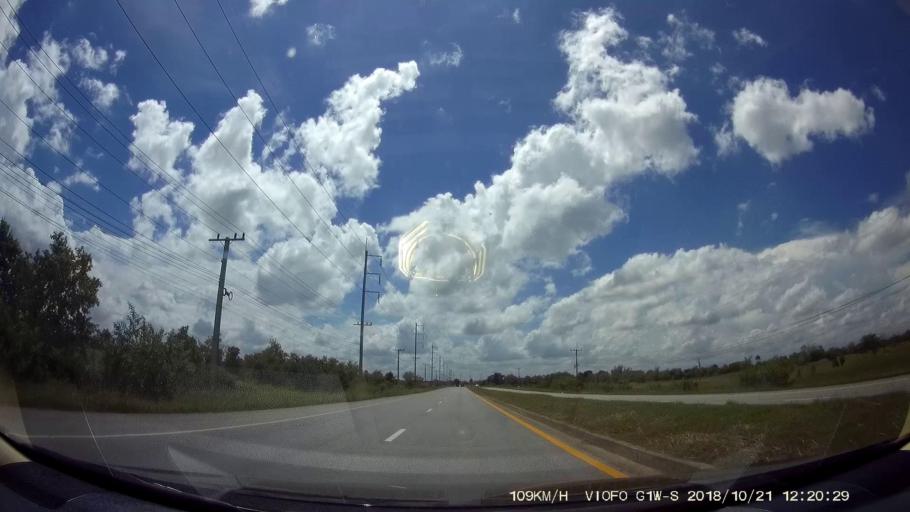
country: TH
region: Nakhon Ratchasima
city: Dan Khun Thot
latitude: 15.2873
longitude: 101.8027
